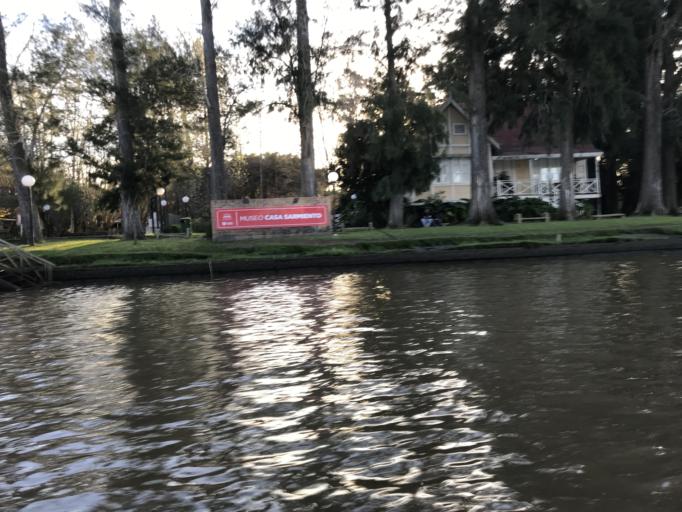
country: AR
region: Buenos Aires
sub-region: Partido de Tigre
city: Tigre
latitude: -34.3827
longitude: -58.5762
